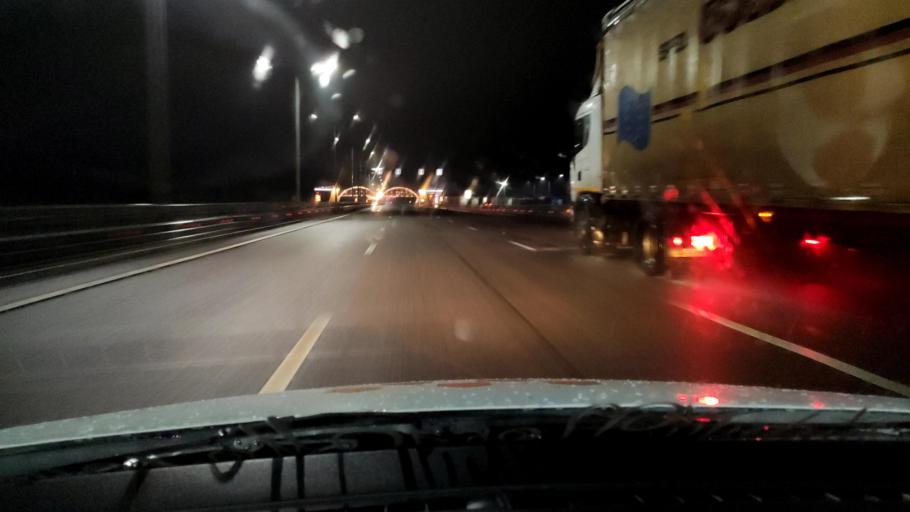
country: RU
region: Voronezj
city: Podgornoye
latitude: 51.8120
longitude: 39.2522
